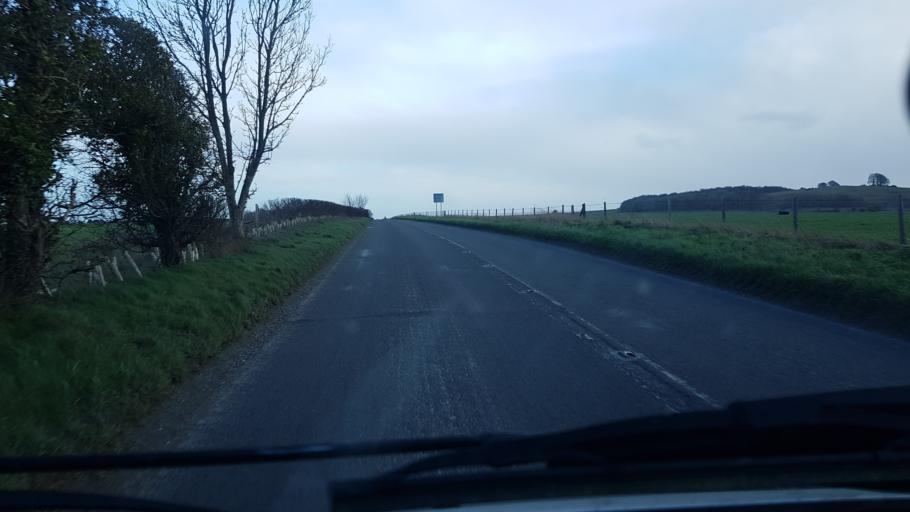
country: GB
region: England
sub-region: Wiltshire
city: Collingbourne Kingston
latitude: 51.2670
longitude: -1.6455
